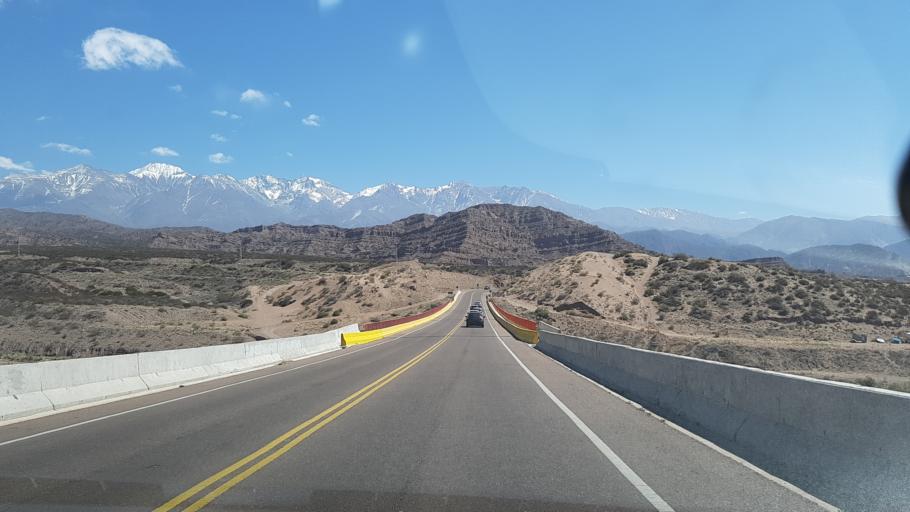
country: AR
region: Mendoza
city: Lujan de Cuyo
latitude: -32.9922
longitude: -69.1634
